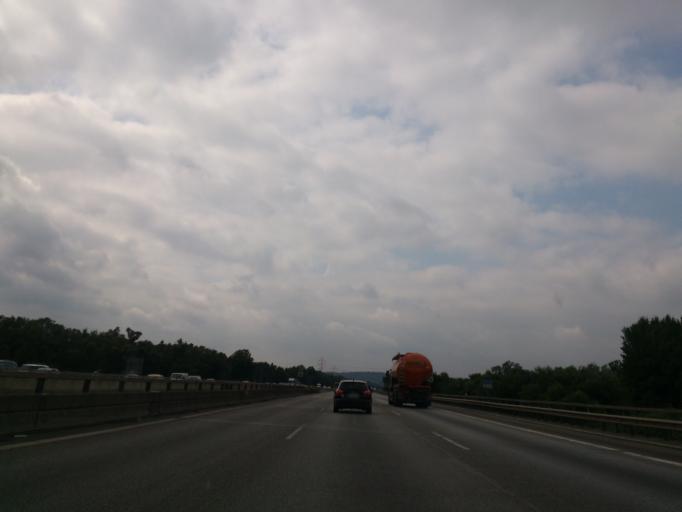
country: DE
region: Hamburg
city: Altona
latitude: 53.5000
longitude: 9.9129
